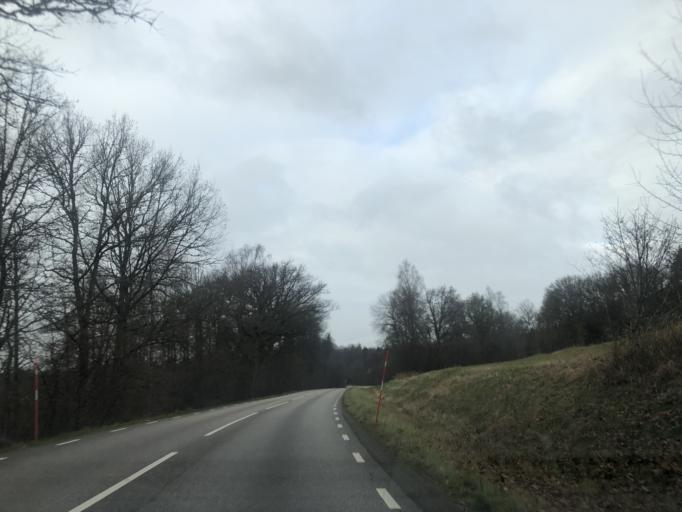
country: SE
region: Vaestra Goetaland
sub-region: Tranemo Kommun
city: Langhem
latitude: 57.6870
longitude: 13.3081
